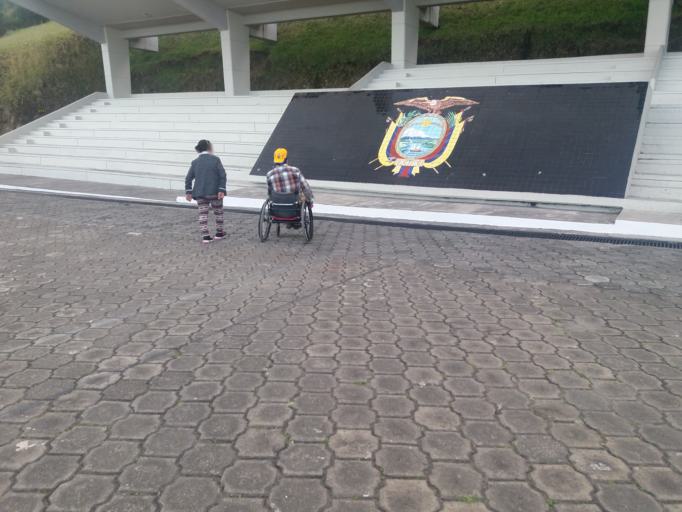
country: EC
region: Pichincha
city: Quito
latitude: -0.2197
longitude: -78.5274
